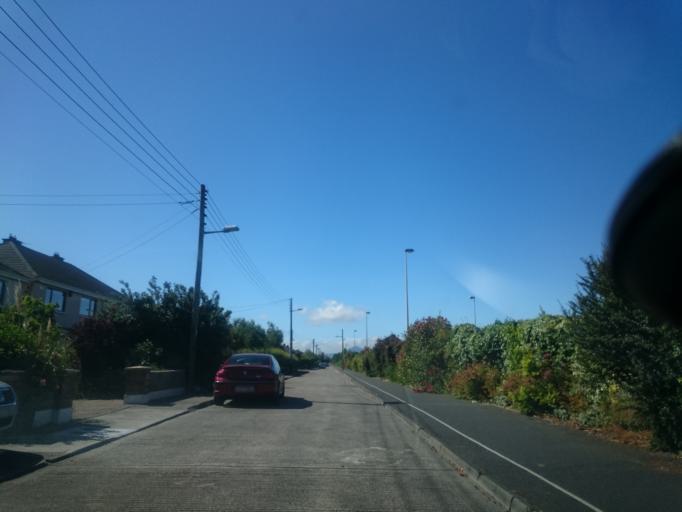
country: IE
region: Leinster
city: Sallynoggin
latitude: 53.2717
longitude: -6.1343
